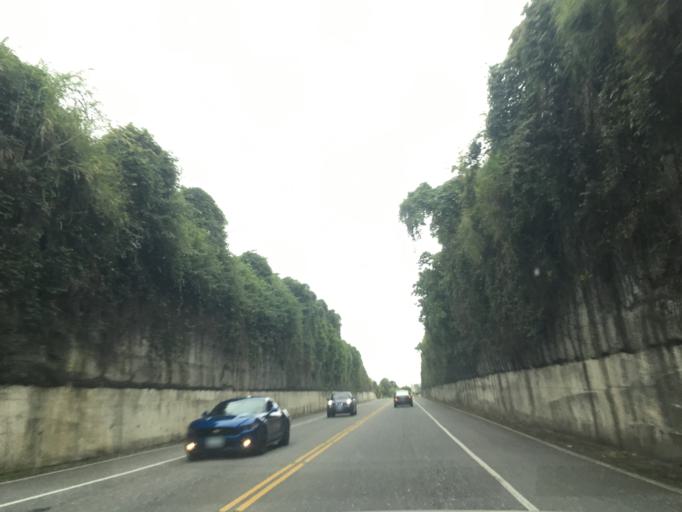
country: TW
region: Taiwan
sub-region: Taitung
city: Taitung
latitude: 23.3143
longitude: 121.4497
